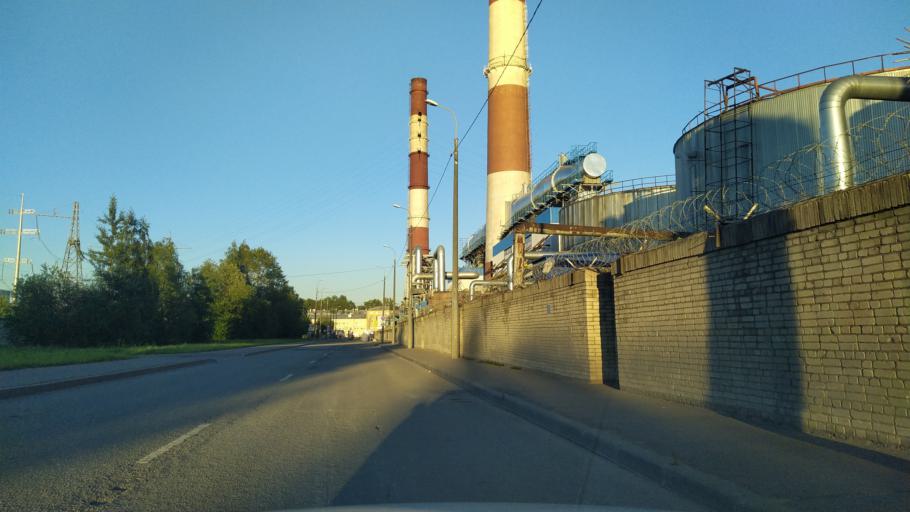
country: RU
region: Leningrad
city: Finlyandskiy
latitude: 59.9713
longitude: 30.3744
